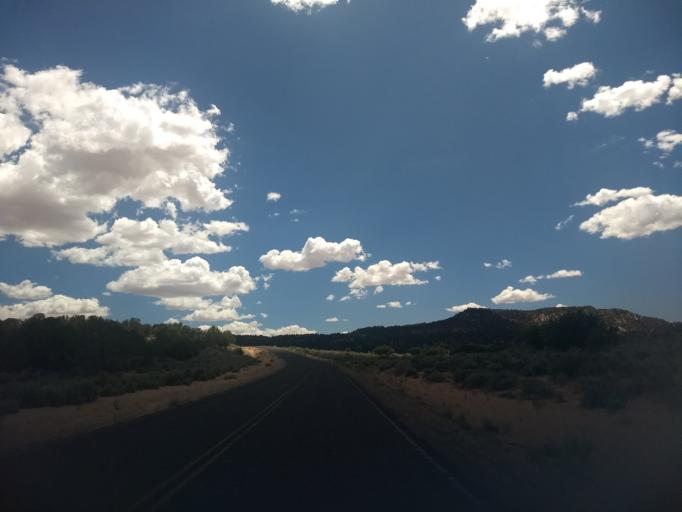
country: US
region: Utah
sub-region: Kane County
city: Kanab
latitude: 37.1280
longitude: -112.6776
